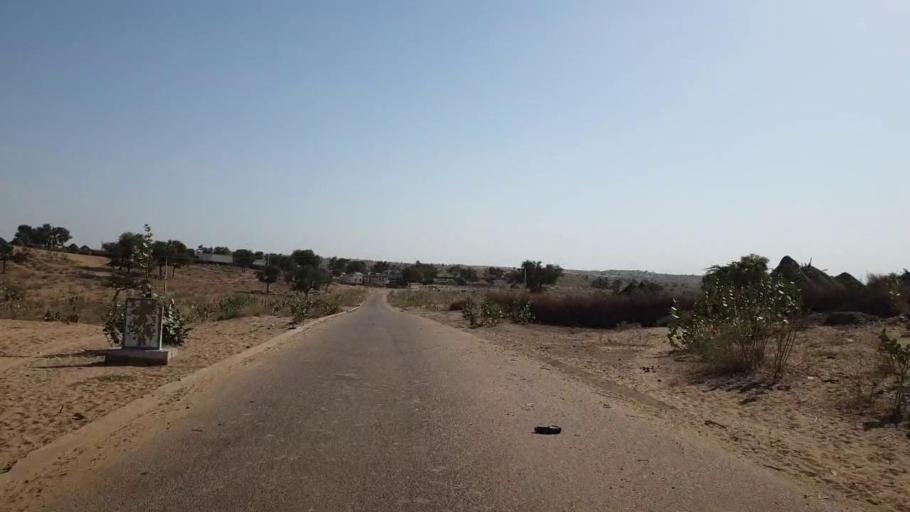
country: PK
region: Sindh
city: Umarkot
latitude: 25.1171
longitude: 70.0426
